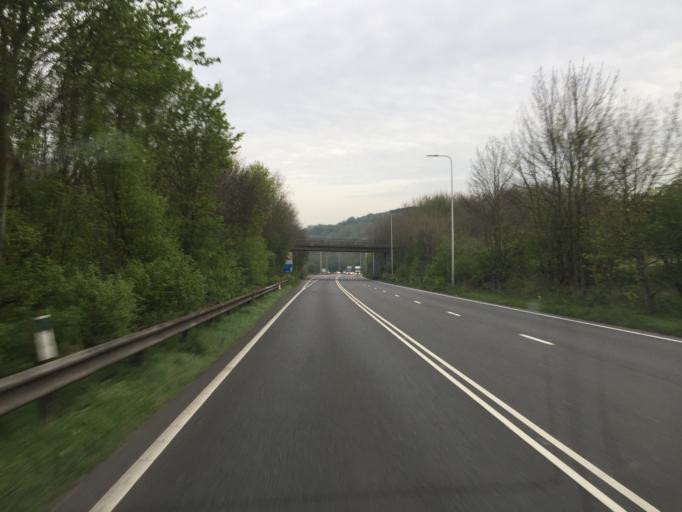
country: GB
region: England
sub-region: Kent
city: Dover
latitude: 51.1351
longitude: 1.3307
